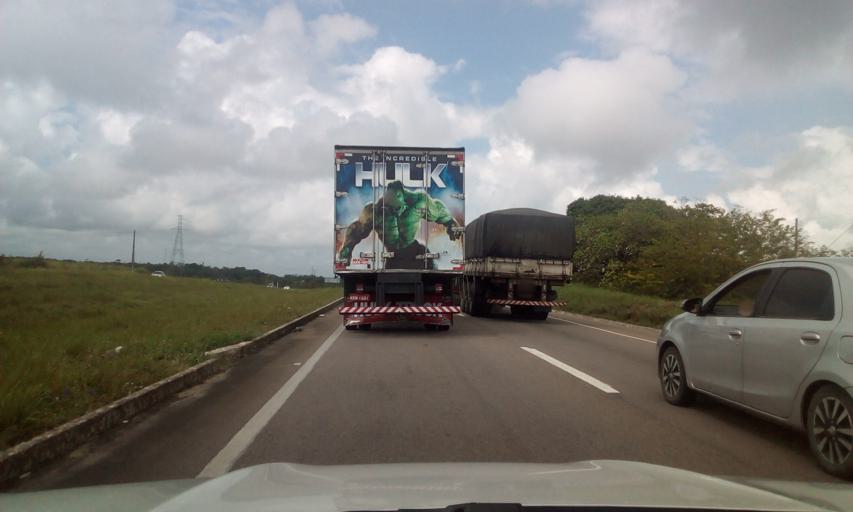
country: BR
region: Paraiba
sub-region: Conde
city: Conde
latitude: -7.3053
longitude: -34.9417
